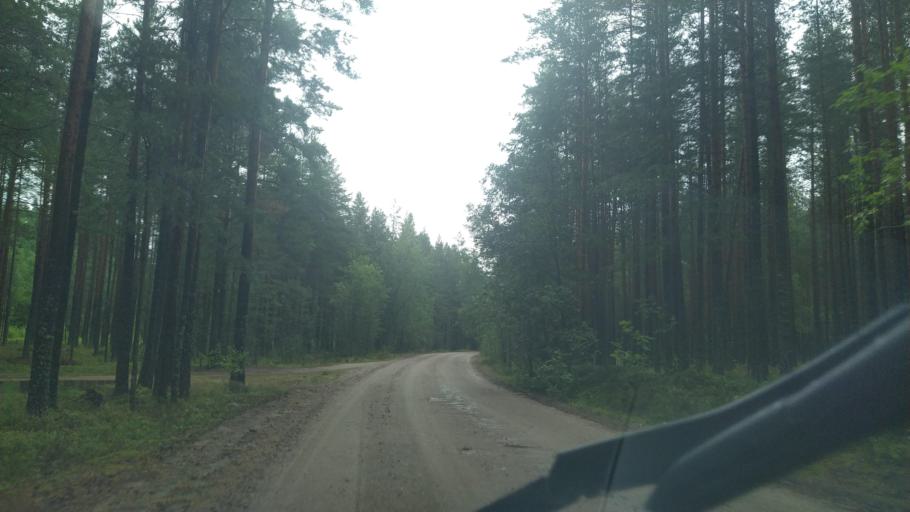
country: RU
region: Leningrad
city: Priozersk
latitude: 60.9683
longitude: 30.2945
